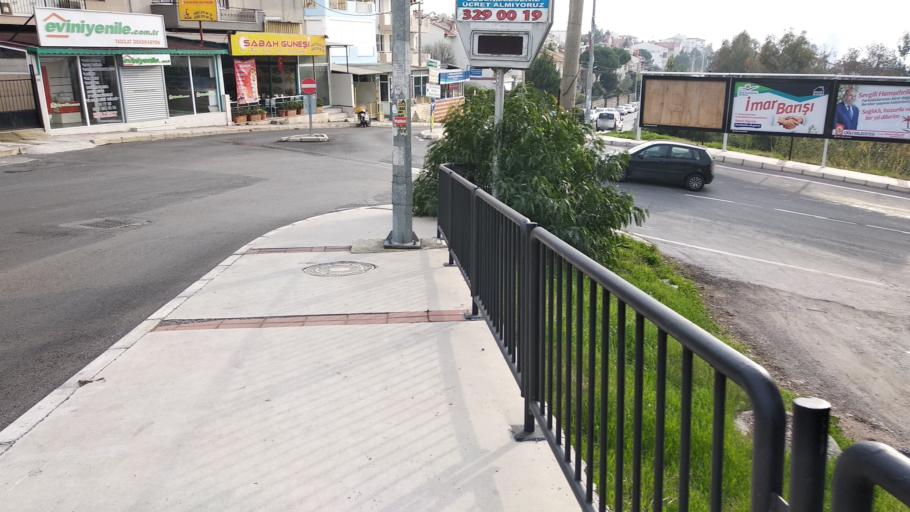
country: TR
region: Izmir
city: Karsiyaka
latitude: 38.4942
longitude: 27.0840
